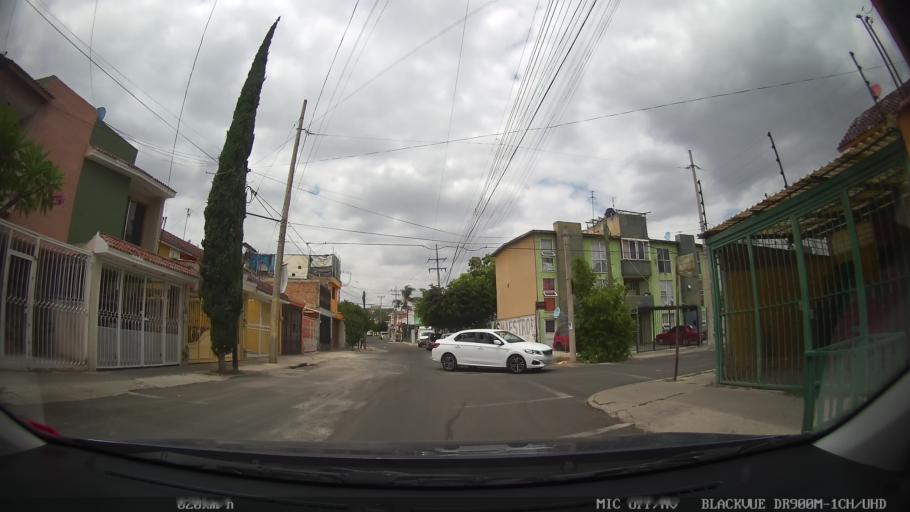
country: MX
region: Jalisco
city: Tonala
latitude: 20.6350
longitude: -103.2610
